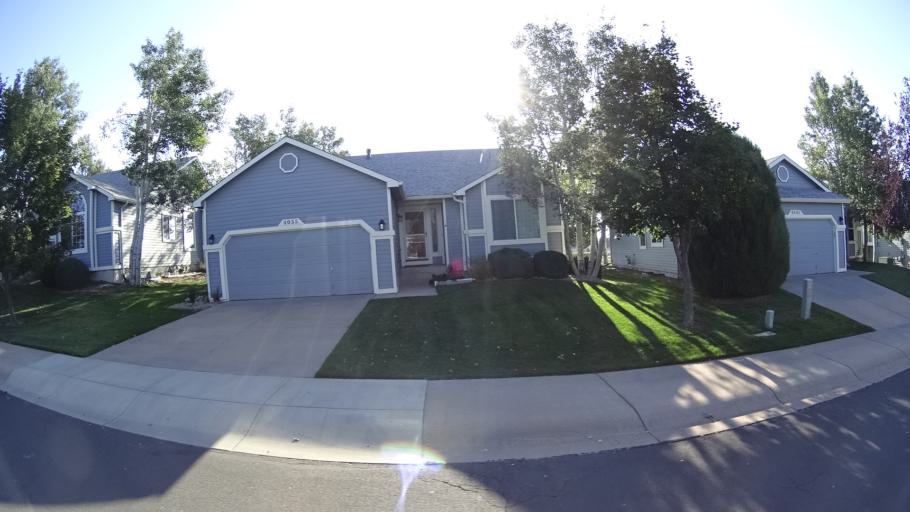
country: US
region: Colorado
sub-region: El Paso County
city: Cimarron Hills
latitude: 38.8900
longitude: -104.7060
